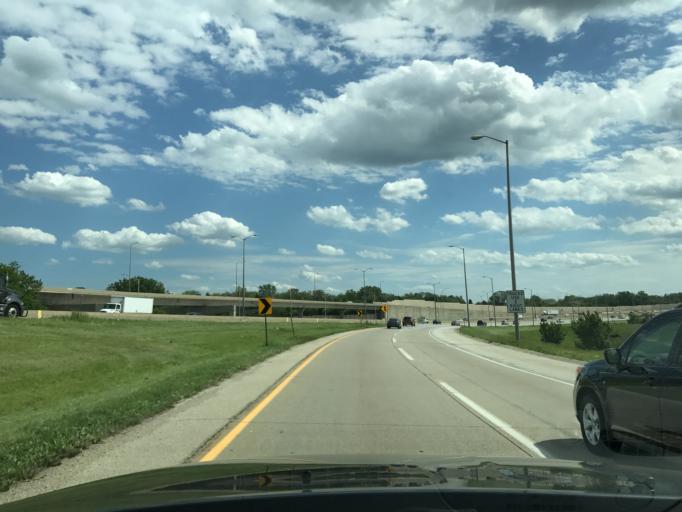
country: US
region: Illinois
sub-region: DuPage County
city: Downers Grove
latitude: 41.8167
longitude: -88.0286
